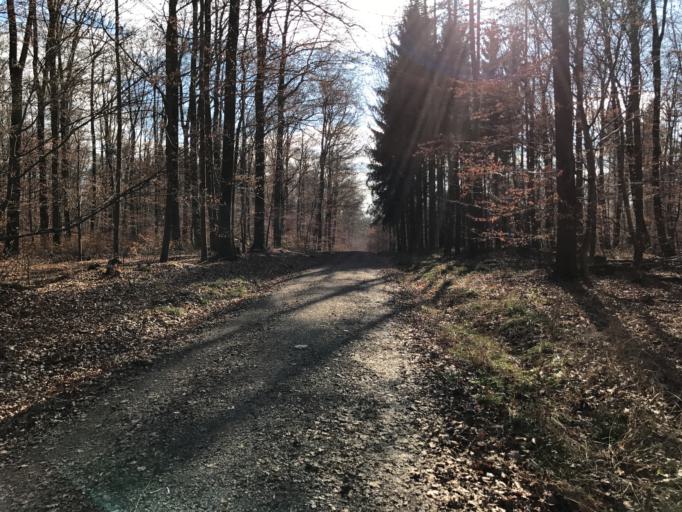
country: DE
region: Hesse
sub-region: Regierungsbezirk Darmstadt
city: Niedernhausen
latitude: 50.1033
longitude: 8.3279
